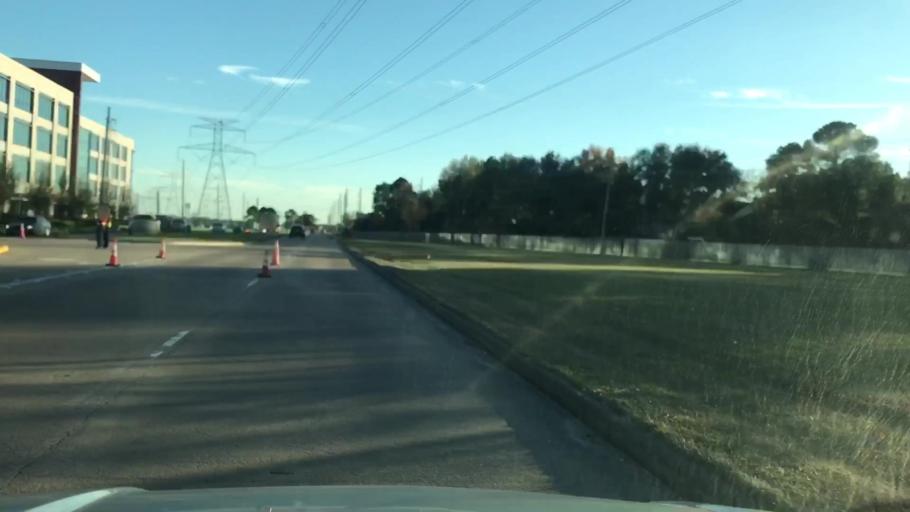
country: US
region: Texas
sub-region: Fort Bend County
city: Cinco Ranch
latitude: 29.7970
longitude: -95.7521
